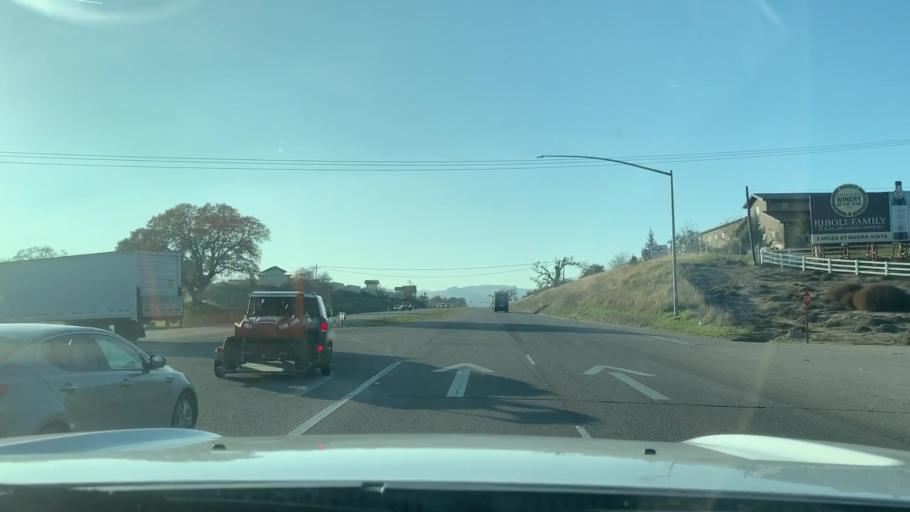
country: US
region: California
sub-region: San Luis Obispo County
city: Paso Robles
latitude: 35.6446
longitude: -120.6492
